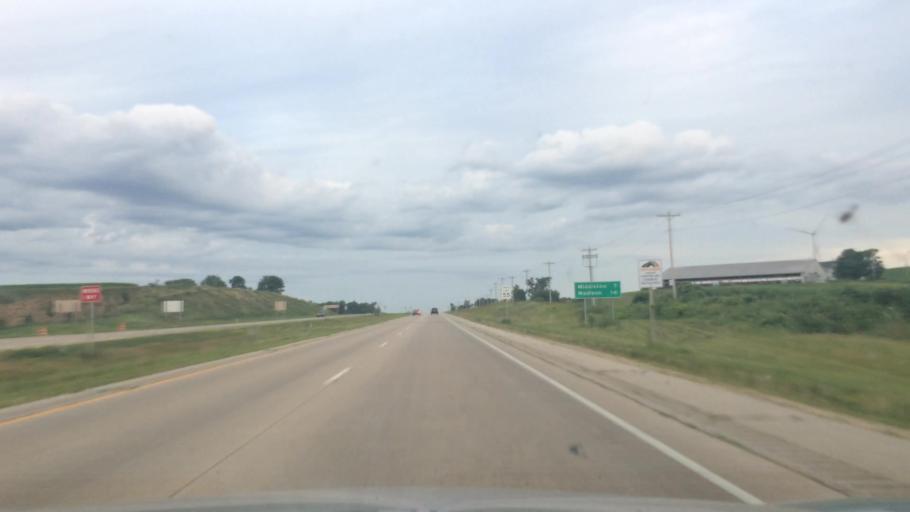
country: US
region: Wisconsin
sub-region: Dane County
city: Waunakee
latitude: 43.1864
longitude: -89.5546
